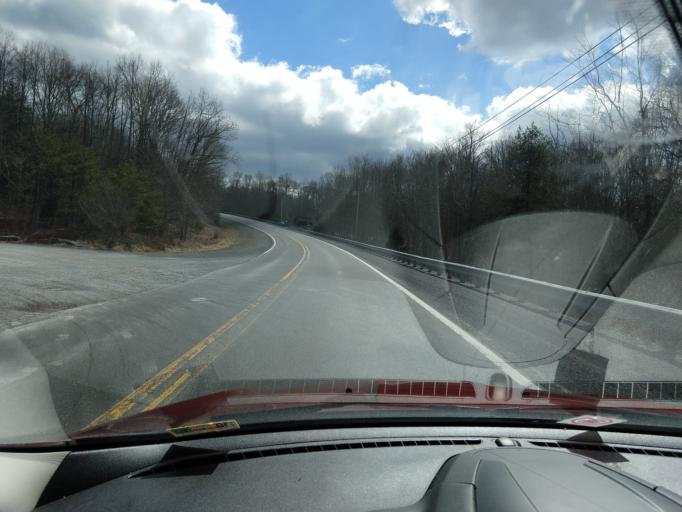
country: US
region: West Virginia
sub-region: Greenbrier County
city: Lewisburg
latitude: 37.8612
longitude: -80.5533
